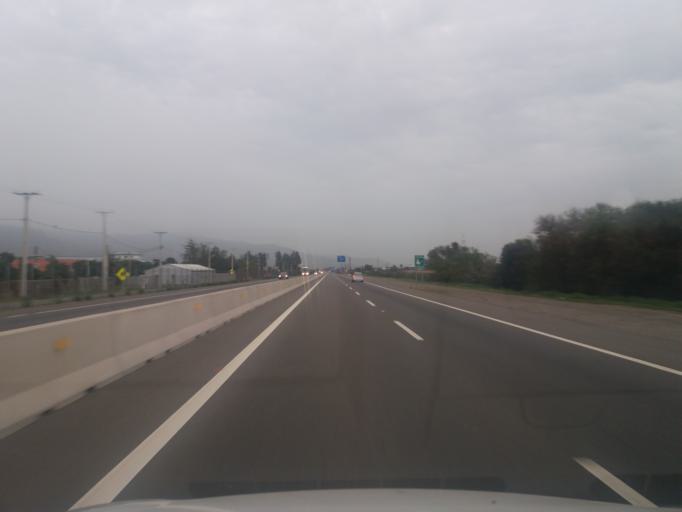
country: CL
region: Valparaiso
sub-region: Provincia de Quillota
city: Quillota
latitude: -32.8647
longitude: -71.2274
